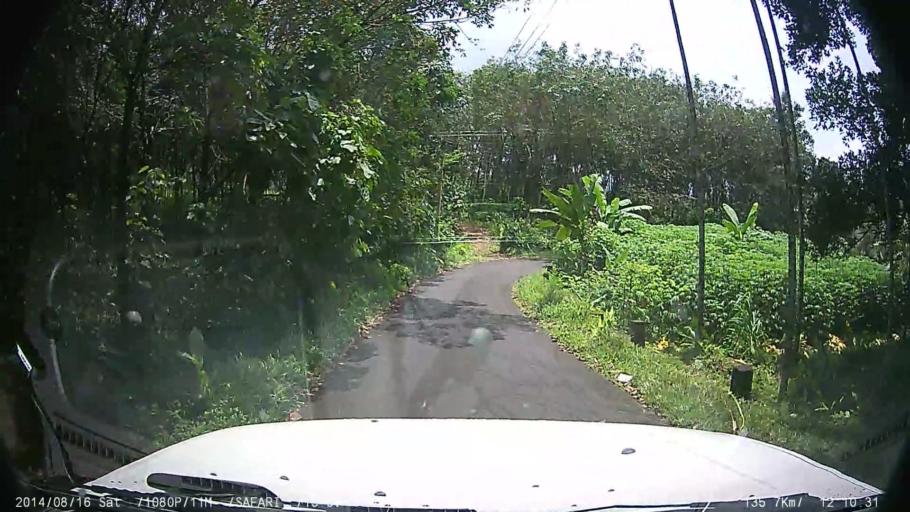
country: IN
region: Kerala
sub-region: Kottayam
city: Palackattumala
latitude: 9.7866
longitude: 76.5541
